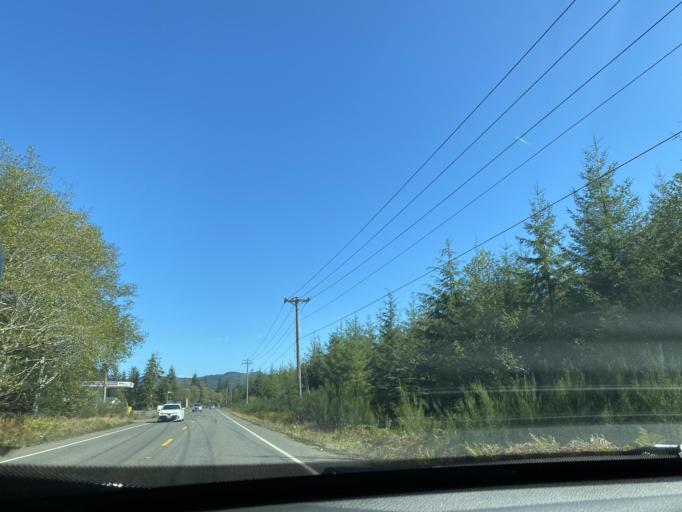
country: US
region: Washington
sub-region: Clallam County
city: Forks
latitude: 47.9654
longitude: -124.4135
